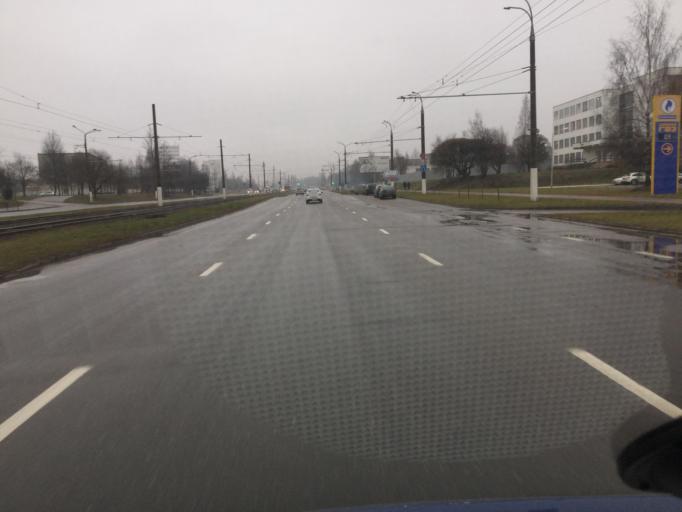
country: BY
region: Vitebsk
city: Vitebsk
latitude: 55.1608
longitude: 30.2365
